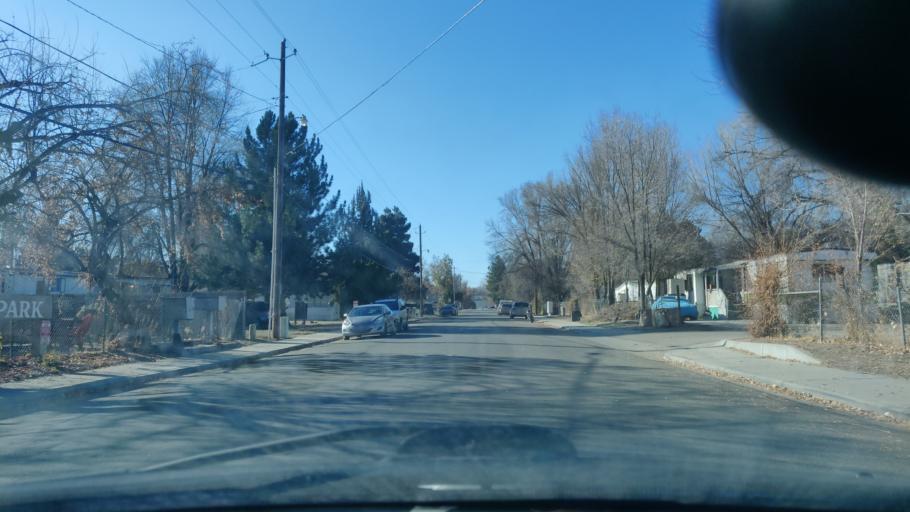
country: US
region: Idaho
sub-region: Ada County
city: Garden City
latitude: 43.6380
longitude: -116.2493
